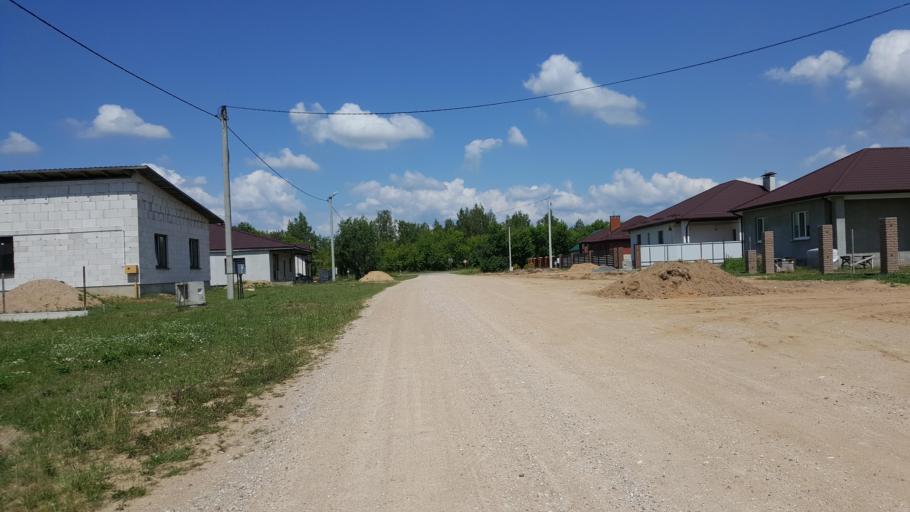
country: BY
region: Brest
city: Kamyanyets
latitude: 52.4016
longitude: 23.8477
